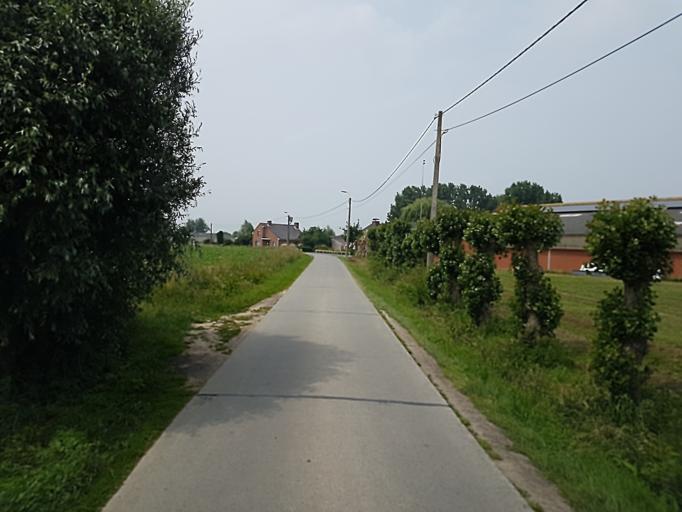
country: BE
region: Flanders
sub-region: Provincie West-Vlaanderen
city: Ardooie
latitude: 50.9578
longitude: 3.1912
